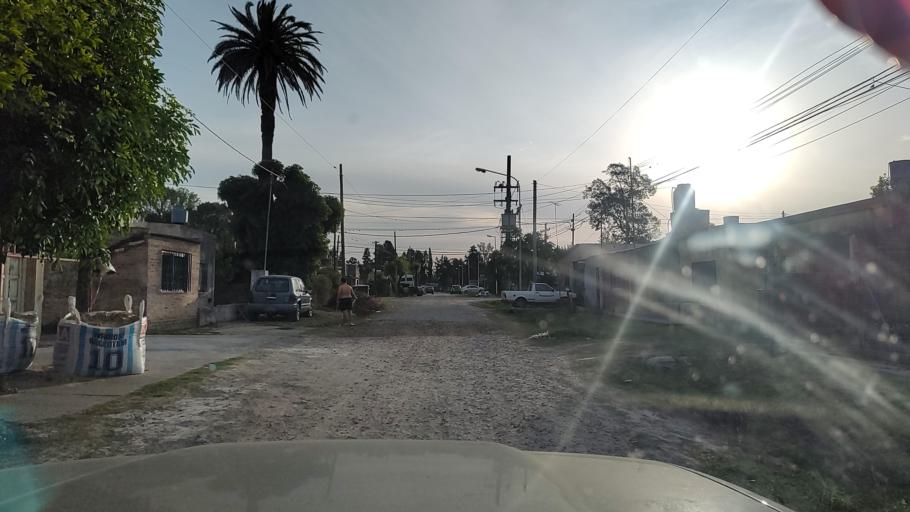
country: AR
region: Buenos Aires
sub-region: Partido de Lujan
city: Lujan
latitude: -34.5704
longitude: -59.1339
